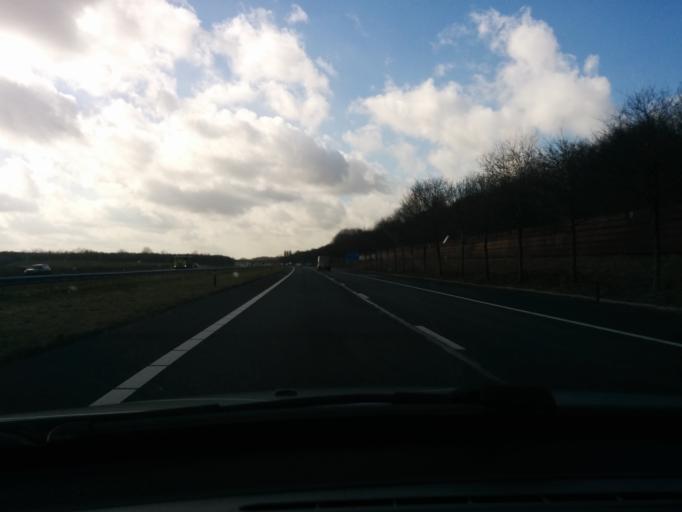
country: NL
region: North Holland
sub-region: Gemeente Huizen
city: Huizen
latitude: 52.2875
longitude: 5.2791
